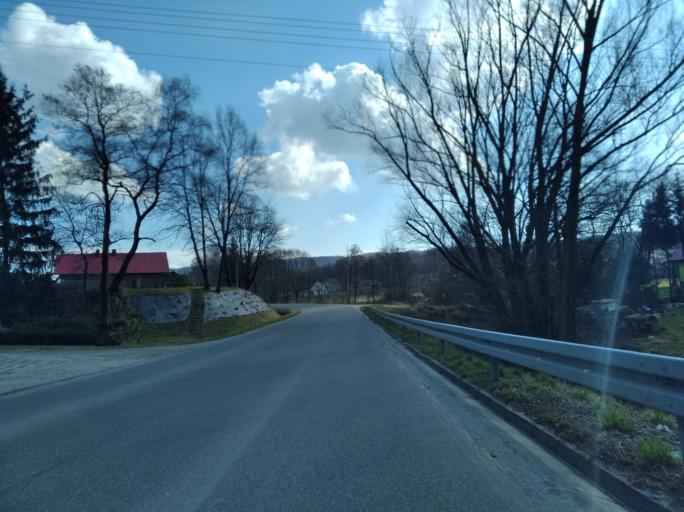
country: PL
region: Subcarpathian Voivodeship
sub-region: Powiat jasielski
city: Kolaczyce
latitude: 49.8577
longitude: 21.4867
